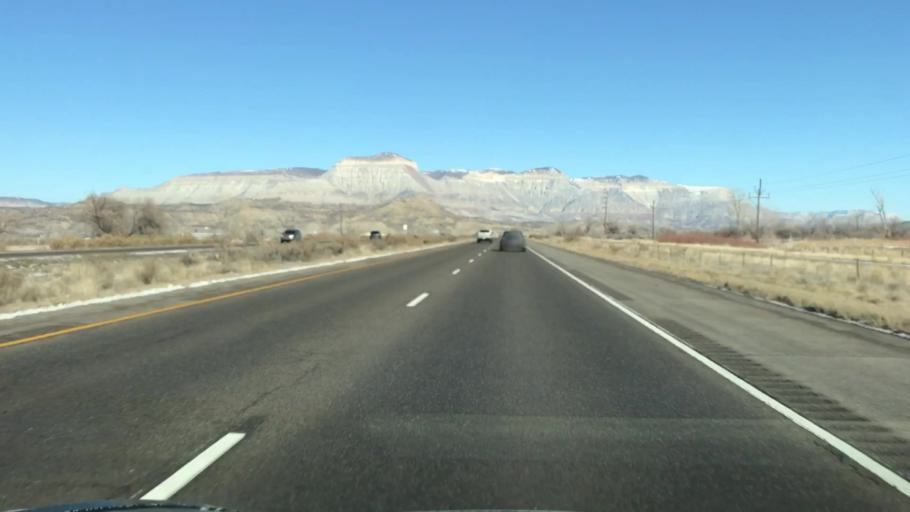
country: US
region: Colorado
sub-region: Garfield County
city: Parachute
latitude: 39.3100
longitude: -108.2147
